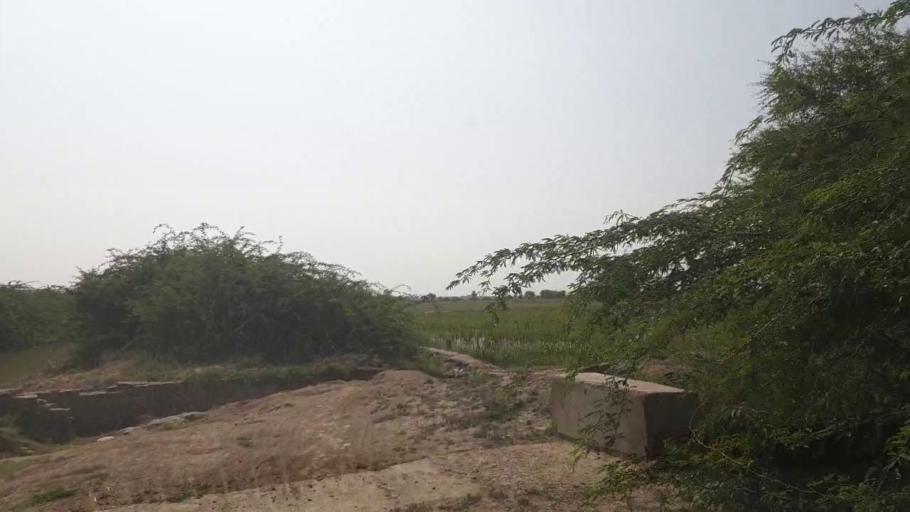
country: PK
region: Sindh
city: Kadhan
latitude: 24.5016
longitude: 68.8497
